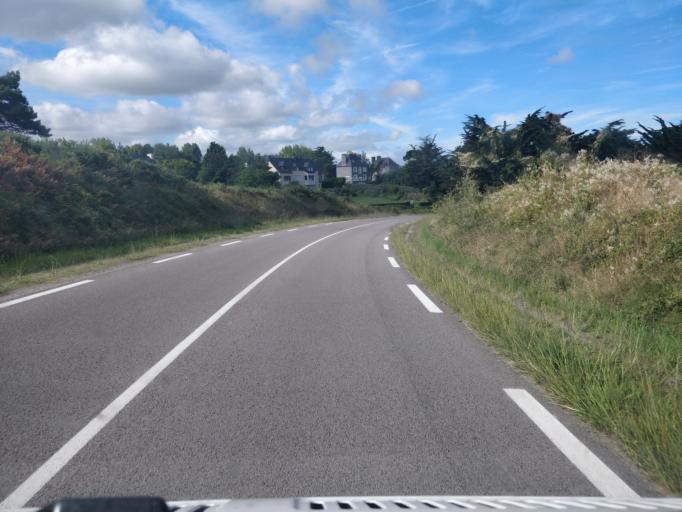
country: FR
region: Brittany
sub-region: Departement des Cotes-d'Armor
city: Plurien
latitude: 48.6418
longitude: -2.3927
